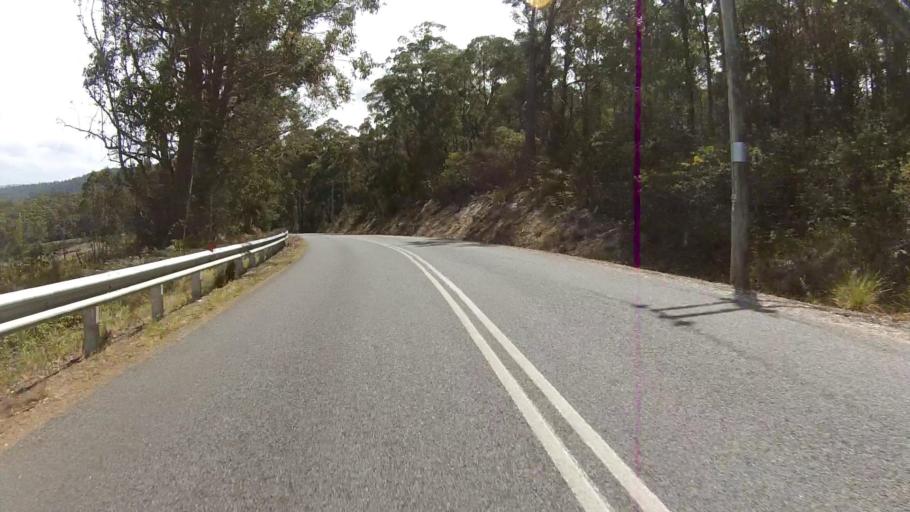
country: AU
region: Tasmania
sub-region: Huon Valley
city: Cygnet
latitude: -43.2244
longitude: 147.1281
